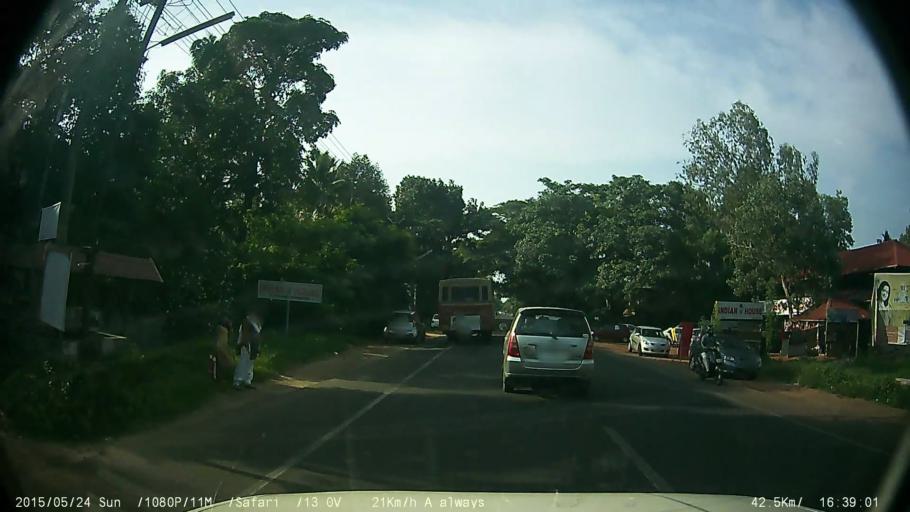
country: IN
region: Kerala
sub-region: Alappuzha
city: Shertallai
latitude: 9.6134
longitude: 76.3303
